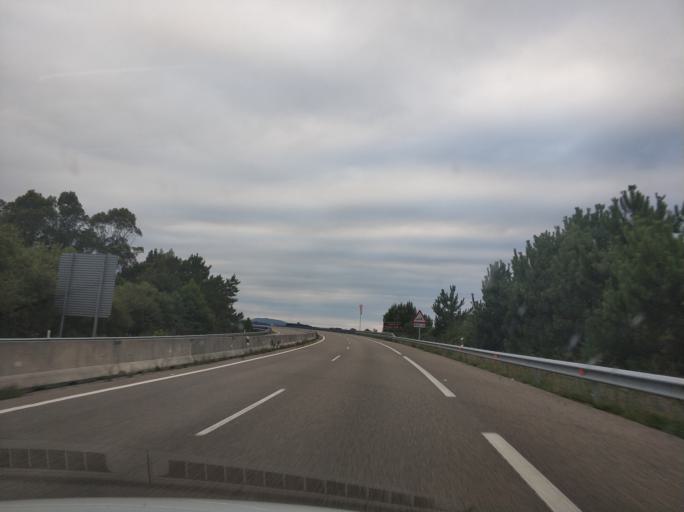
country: ES
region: Asturias
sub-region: Province of Asturias
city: Tineo
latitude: 43.5482
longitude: -6.4615
